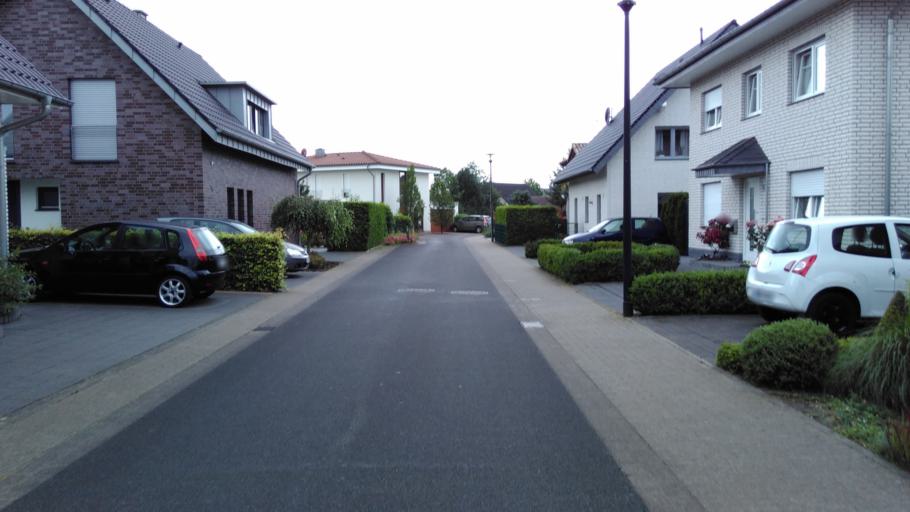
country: DE
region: North Rhine-Westphalia
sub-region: Regierungsbezirk Detmold
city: Verl
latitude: 51.8747
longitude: 8.4962
